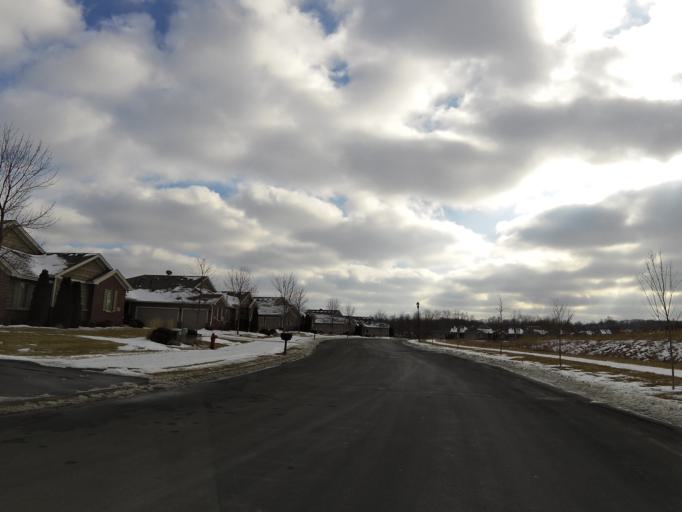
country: US
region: Minnesota
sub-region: Scott County
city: Prior Lake
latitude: 44.7454
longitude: -93.4460
